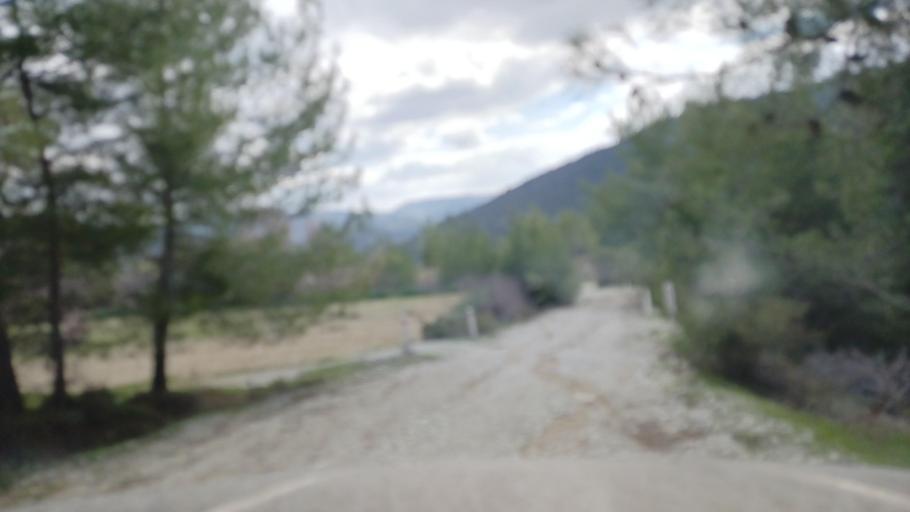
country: CY
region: Limassol
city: Pachna
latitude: 34.8405
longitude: 32.7139
